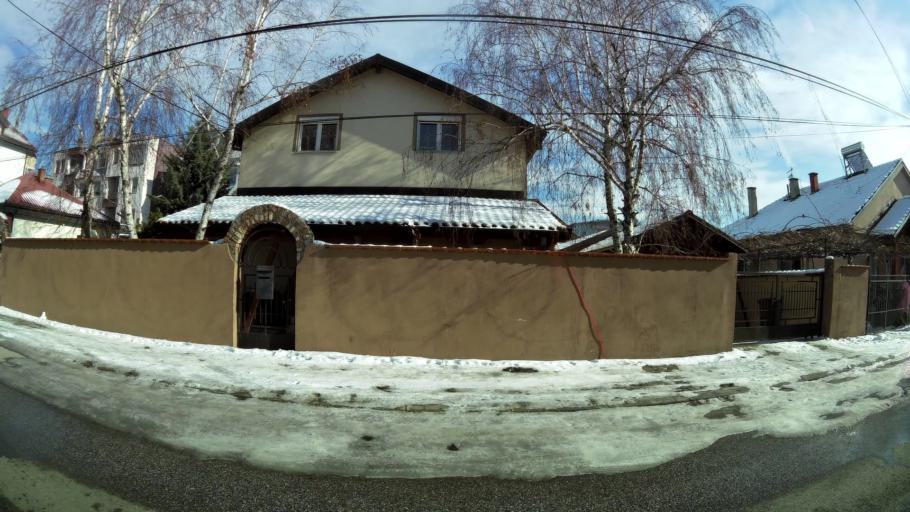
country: MK
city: Krushopek
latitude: 42.0027
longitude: 21.3693
